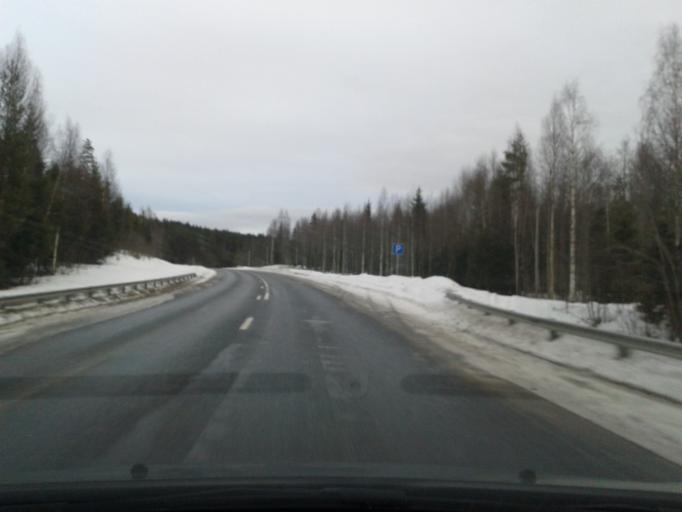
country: SE
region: Vaesternorrland
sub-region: Solleftea Kommun
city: As
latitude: 63.4154
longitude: 16.9607
